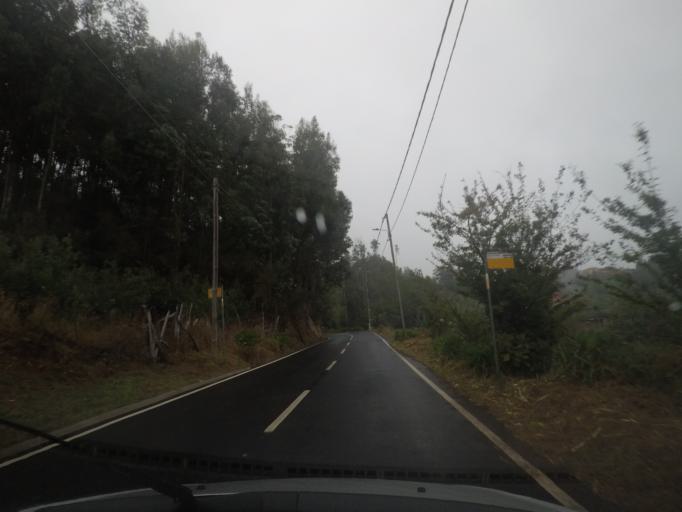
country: PT
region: Madeira
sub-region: Santa Cruz
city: Camacha
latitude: 32.6957
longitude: -16.8381
